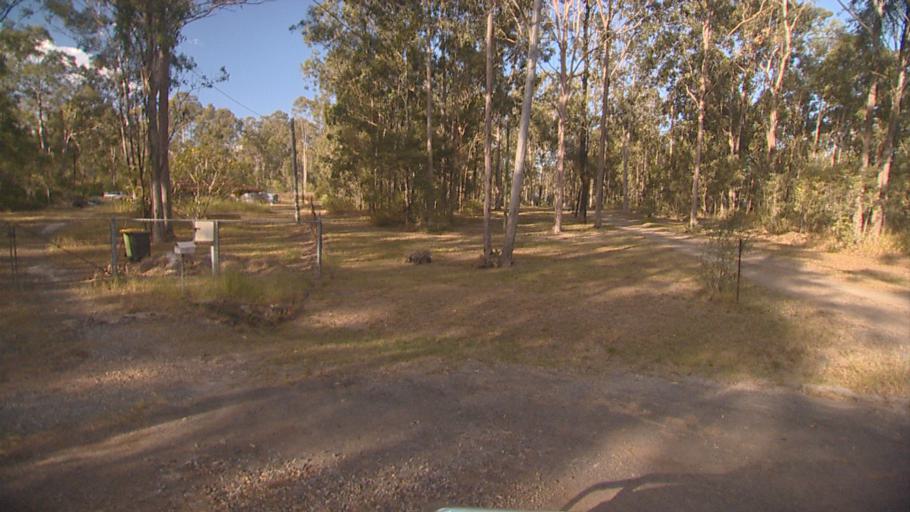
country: AU
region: Queensland
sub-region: Ipswich
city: Springfield Lakes
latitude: -27.6939
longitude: 152.9625
